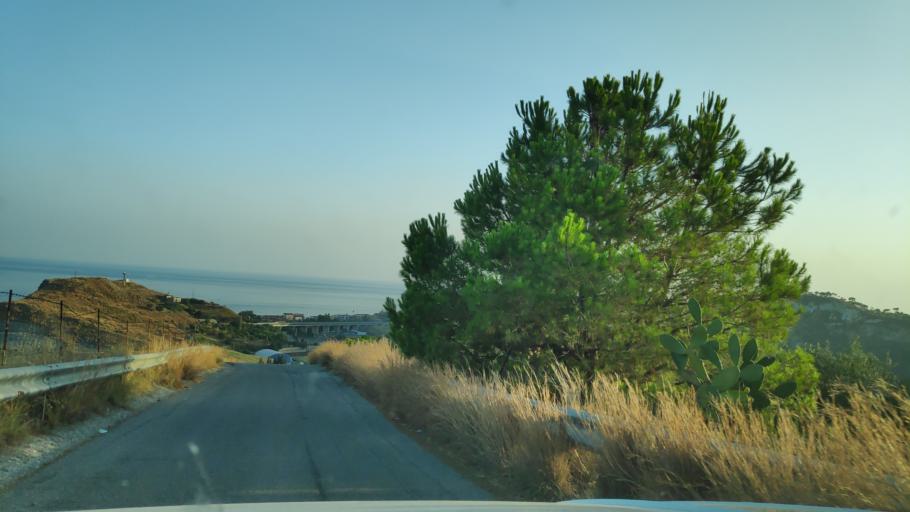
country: IT
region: Calabria
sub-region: Provincia di Reggio Calabria
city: Bova Marina
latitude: 37.9408
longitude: 15.9145
